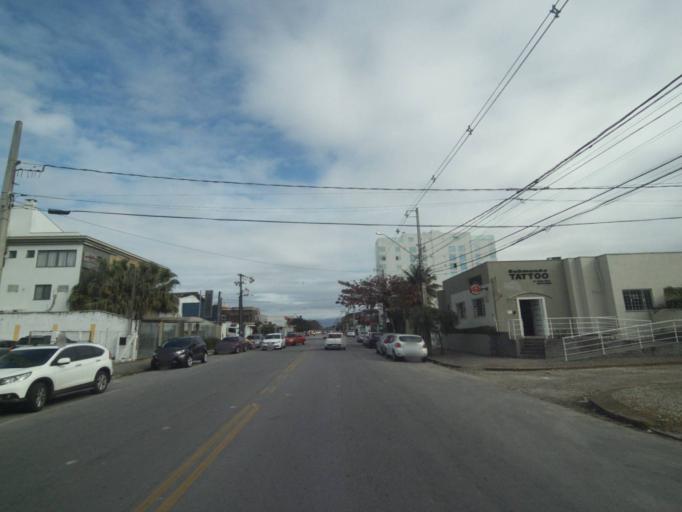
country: BR
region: Parana
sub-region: Paranagua
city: Paranagua
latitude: -25.5168
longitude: -48.5133
